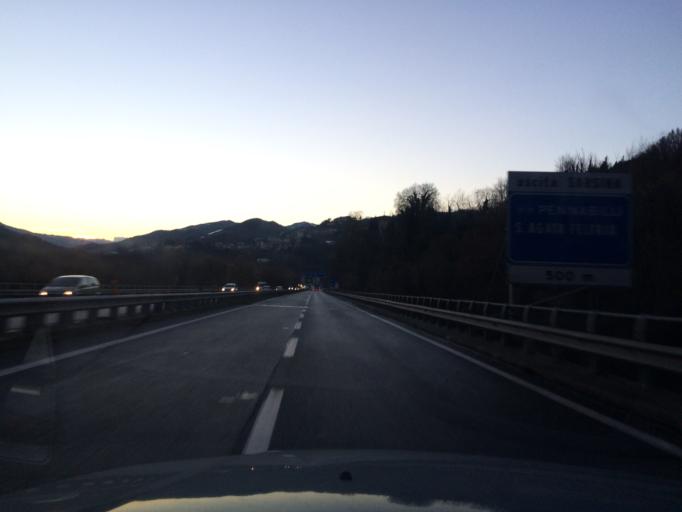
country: IT
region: Emilia-Romagna
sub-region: Forli-Cesena
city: Sarsina
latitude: 43.9237
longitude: 12.1631
